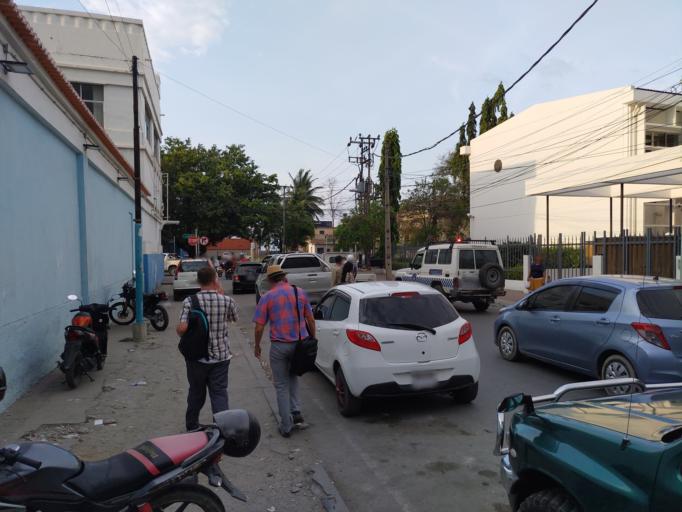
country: TL
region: Dili
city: Dili
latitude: -8.5551
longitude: 125.5757
